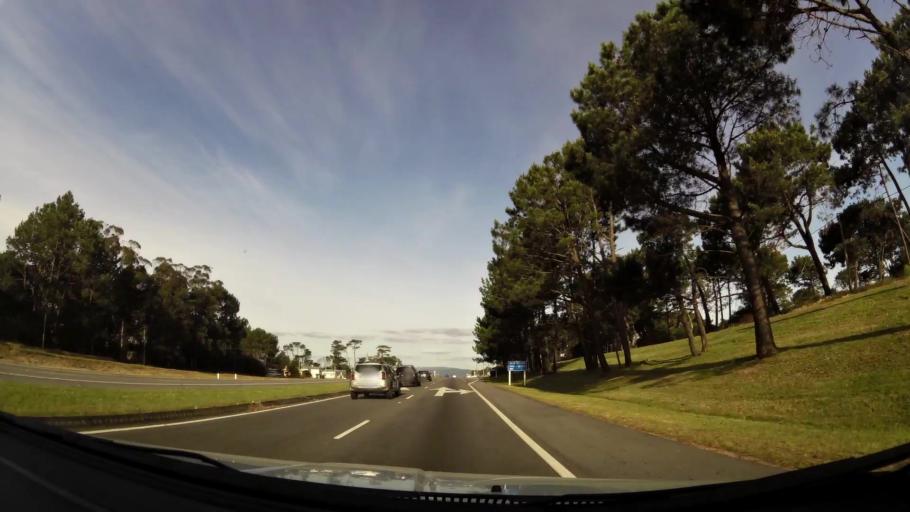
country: UY
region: Lavalleja
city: Solis de Mataojo
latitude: -34.7837
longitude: -55.4934
